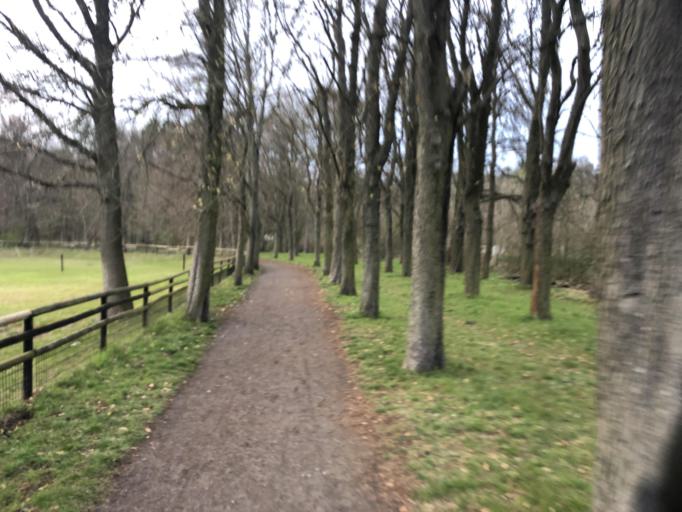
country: DE
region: Berlin
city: Frohnau
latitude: 52.6456
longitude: 13.2911
